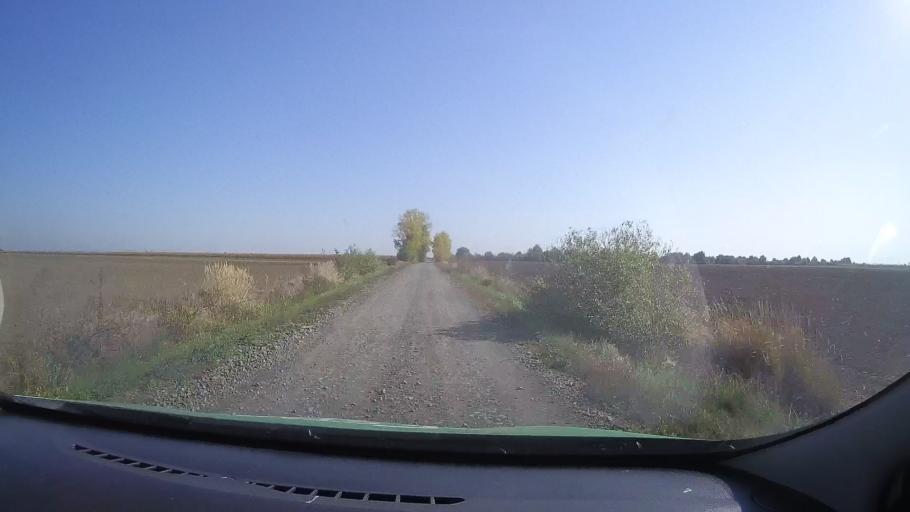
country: RO
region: Satu Mare
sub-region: Comuna Urziceni
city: Urziceni
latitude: 47.7361
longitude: 22.4340
